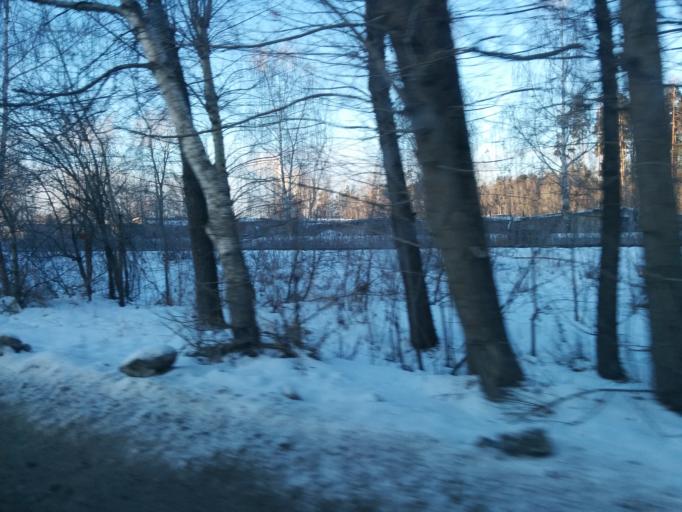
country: RU
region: Perm
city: Overyata
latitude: 58.0152
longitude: 55.9587
